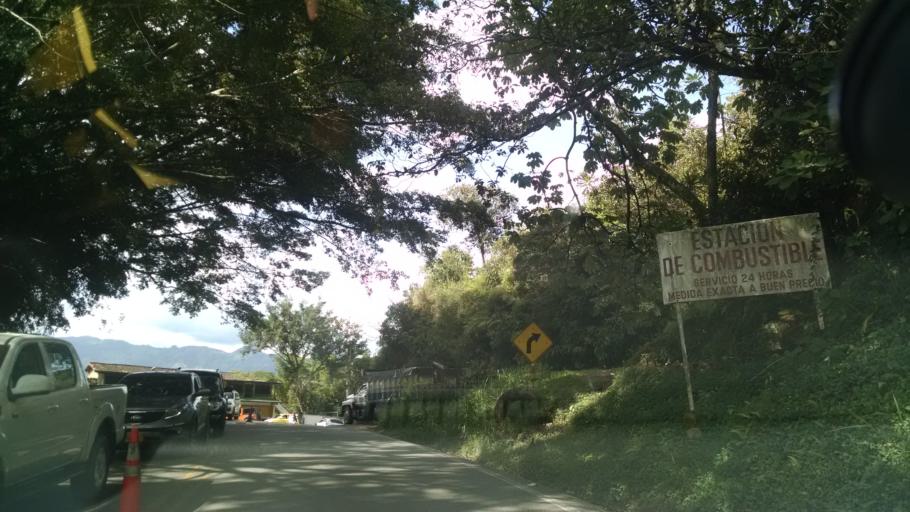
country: CO
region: Antioquia
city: Santo Domingo
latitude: 6.5318
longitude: -75.2363
